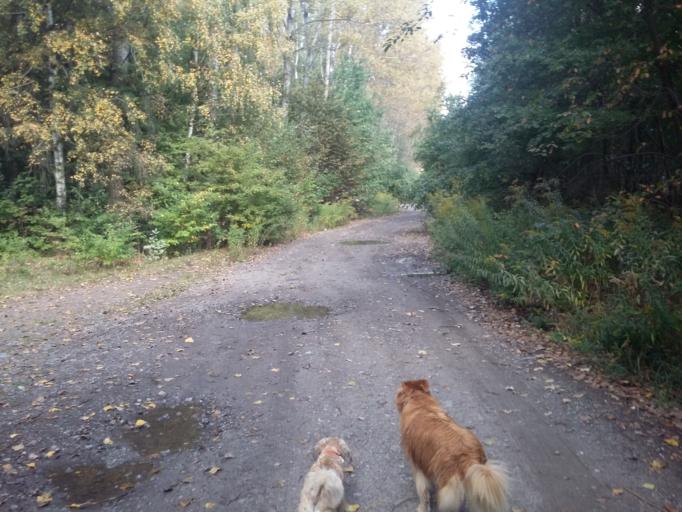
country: PL
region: Lodz Voivodeship
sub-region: Powiat pabianicki
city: Ksawerow
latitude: 51.7261
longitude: 19.3966
